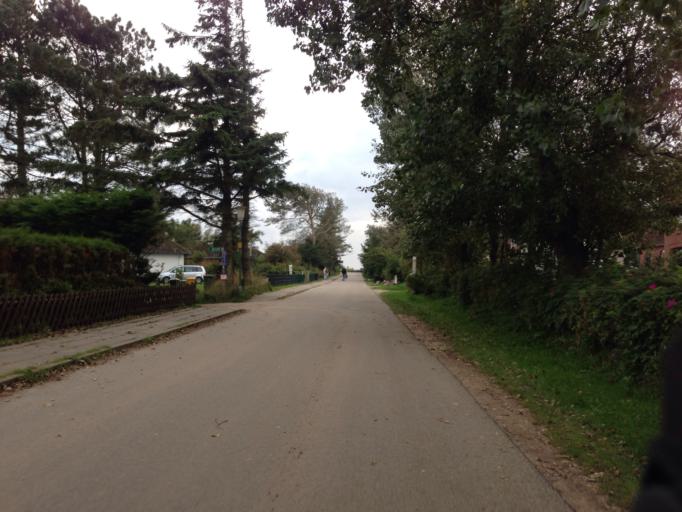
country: DE
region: Schleswig-Holstein
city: Borgsum
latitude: 54.6862
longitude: 8.4685
